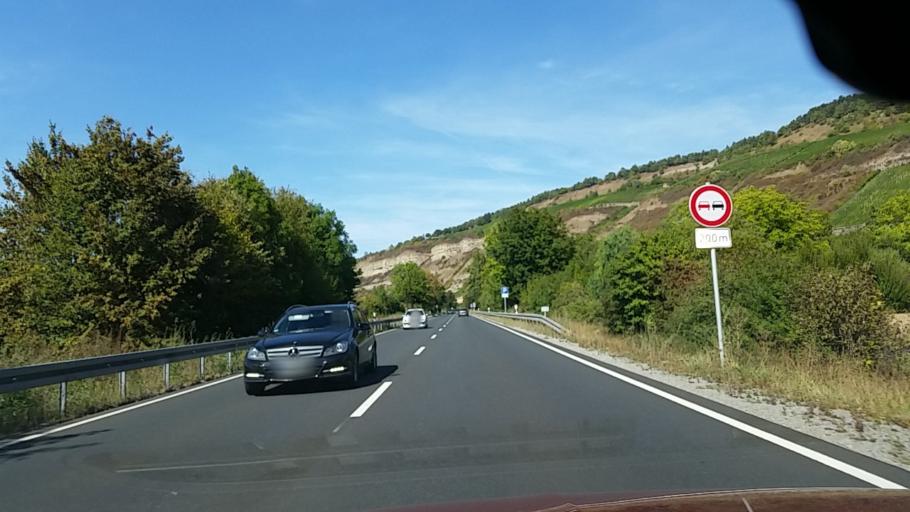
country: DE
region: Bavaria
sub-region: Regierungsbezirk Unterfranken
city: Thungersheim
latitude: 49.8890
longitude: 9.8363
